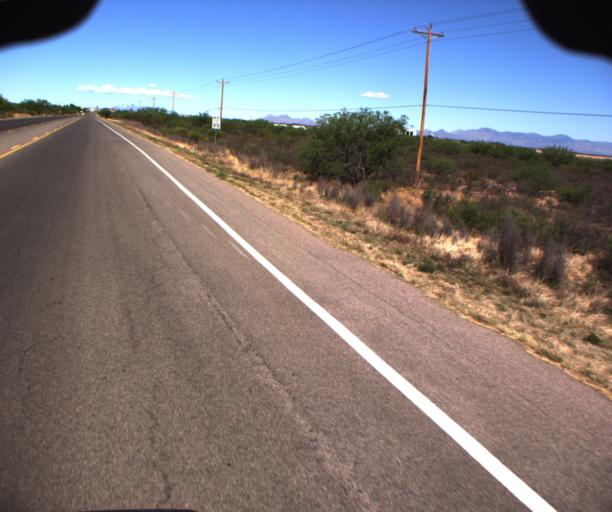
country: US
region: Arizona
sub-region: Cochise County
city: Sierra Vista Southeast
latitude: 31.5522
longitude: -110.1923
